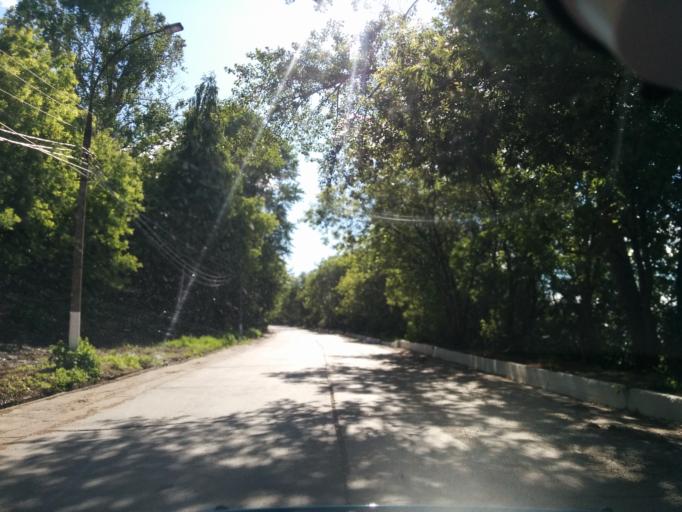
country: RU
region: Perm
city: Perm
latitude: 58.0142
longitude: 56.2084
